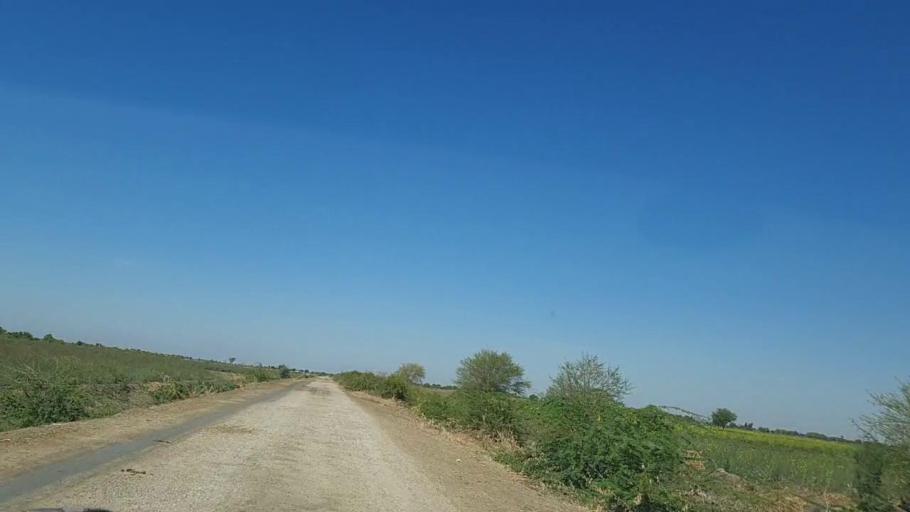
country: PK
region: Sindh
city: Dhoro Naro
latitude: 25.5398
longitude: 69.5000
